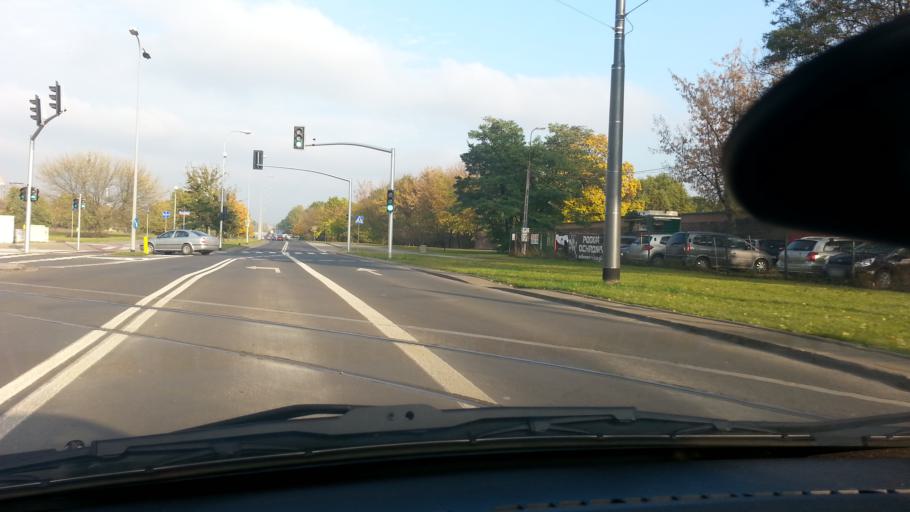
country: PL
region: Masovian Voivodeship
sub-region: Warszawa
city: Targowek
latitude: 52.2830
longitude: 21.0339
